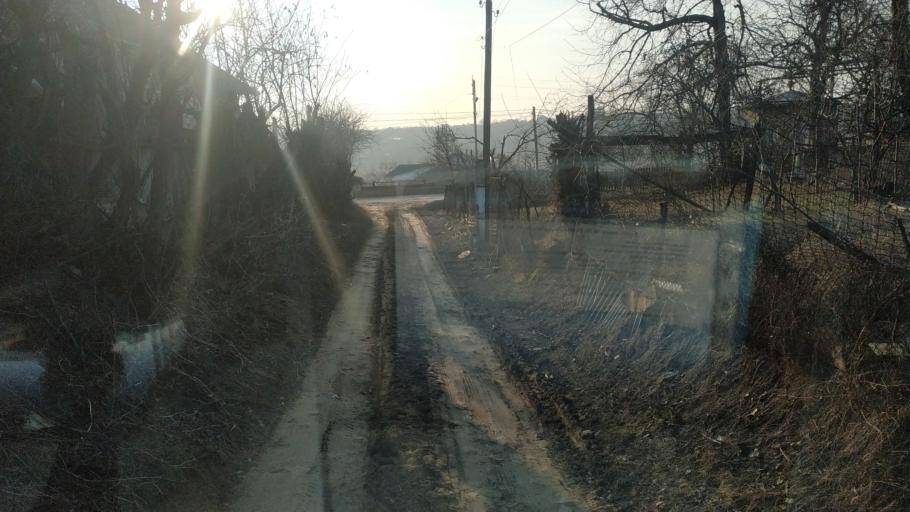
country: MD
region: Hincesti
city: Dancu
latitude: 46.7727
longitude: 28.3543
